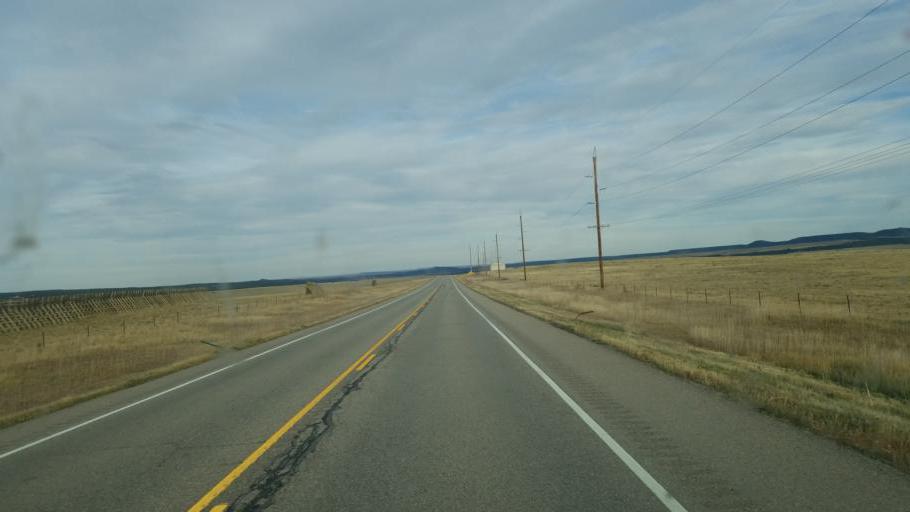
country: US
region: Colorado
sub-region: Huerfano County
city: Walsenburg
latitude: 37.5473
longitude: -104.9923
